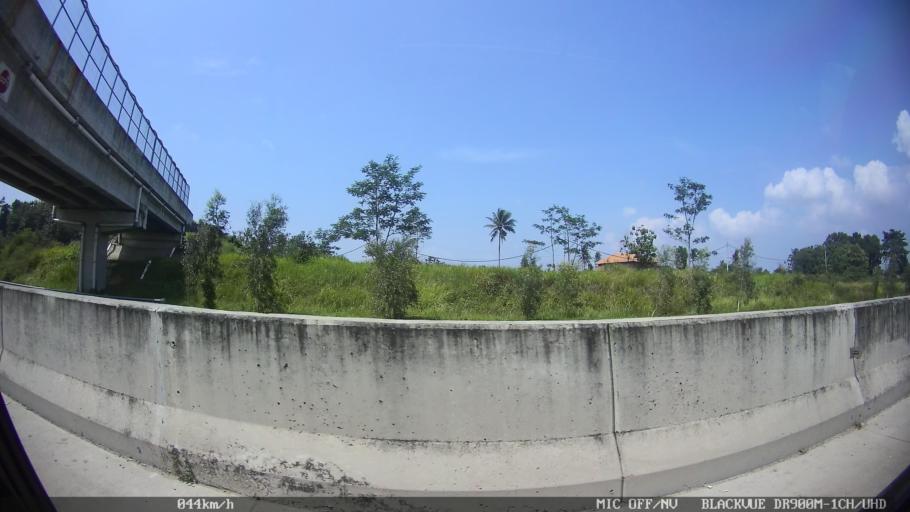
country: ID
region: Lampung
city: Kedaton
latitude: -5.3209
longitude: 105.2701
